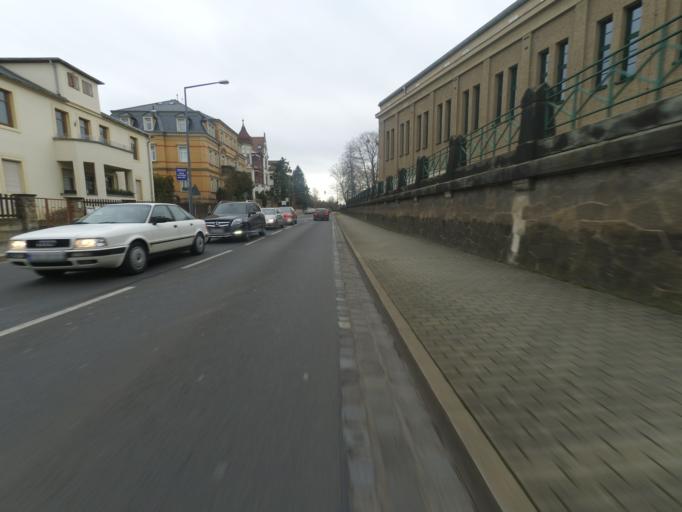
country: DE
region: Saxony
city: Albertstadt
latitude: 51.0344
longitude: 13.8232
